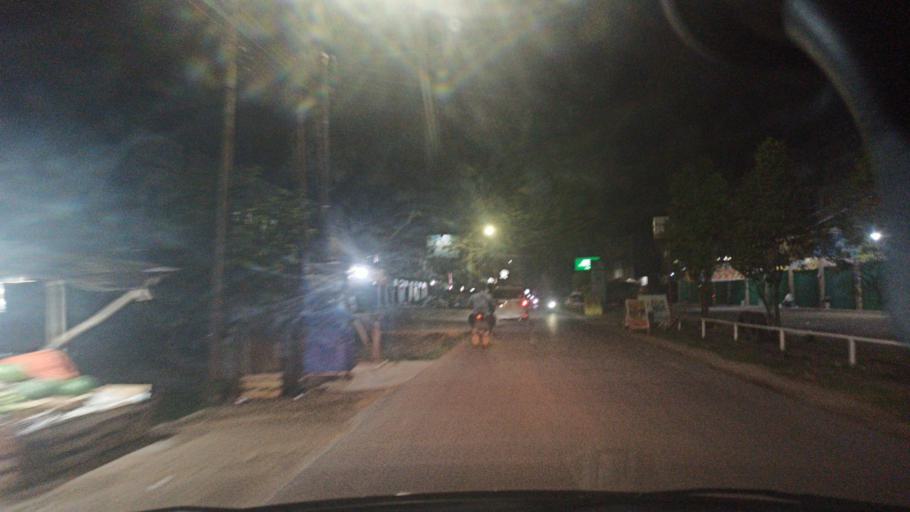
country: ID
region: South Sumatra
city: Palembang
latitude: -2.9223
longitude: 104.7852
